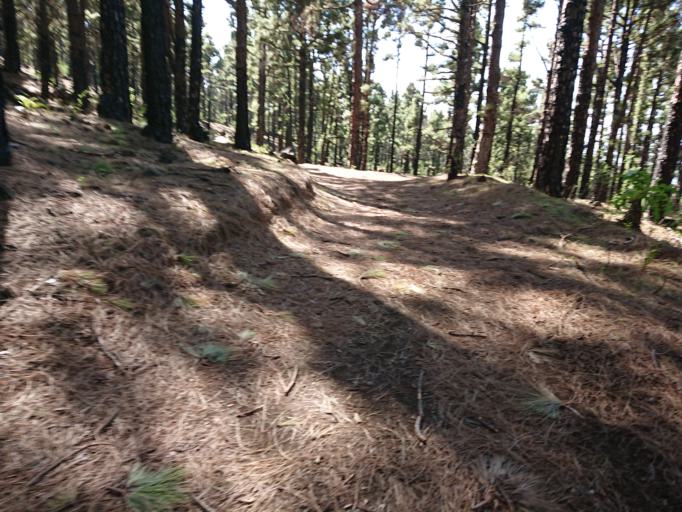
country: ES
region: Canary Islands
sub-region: Provincia de Santa Cruz de Tenerife
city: El Paso
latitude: 28.5945
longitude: -17.8619
